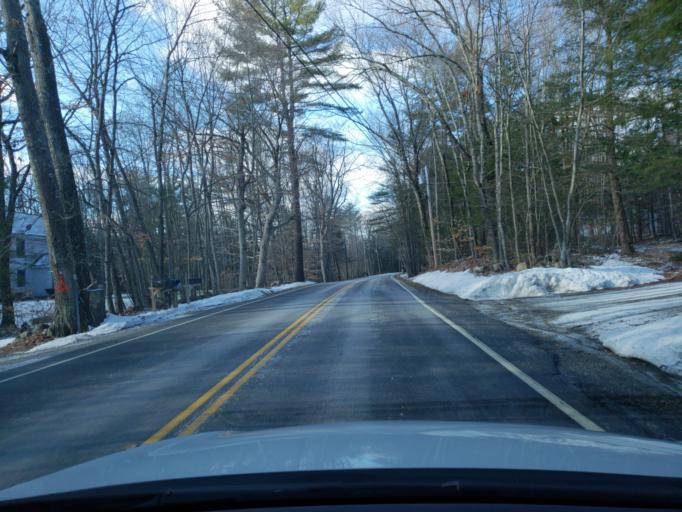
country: US
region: New Hampshire
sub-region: Hillsborough County
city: New Boston
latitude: 42.9916
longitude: -71.7394
